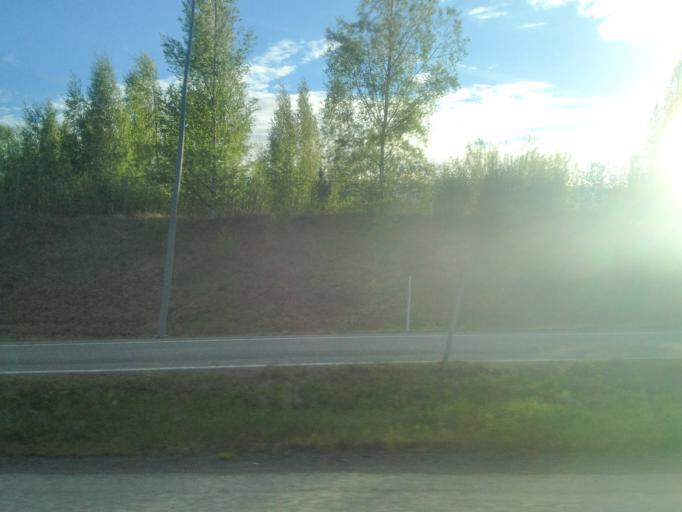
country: FI
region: Pirkanmaa
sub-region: Etelae-Pirkanmaa
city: Toijala
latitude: 61.2180
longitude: 23.8390
